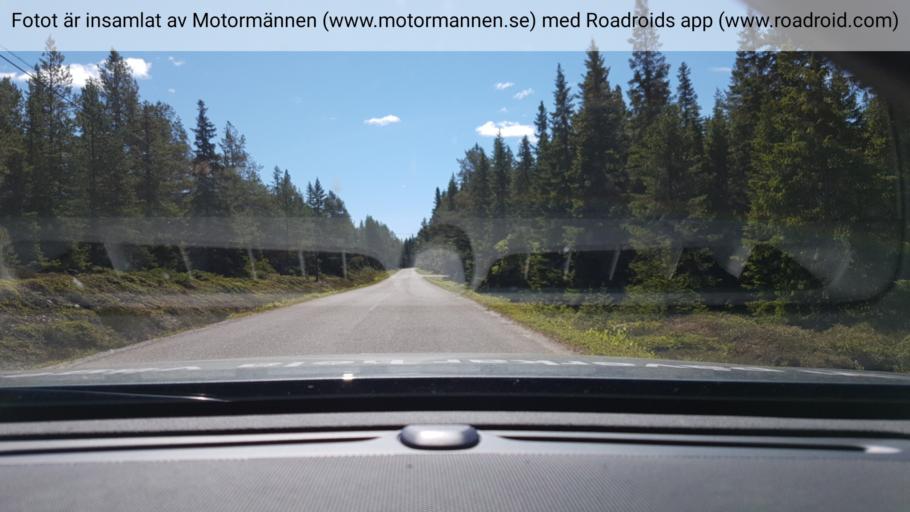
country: SE
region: Vaesterbotten
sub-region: Skelleftea Kommun
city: Skelleftehamn
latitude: 64.4710
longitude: 21.5829
